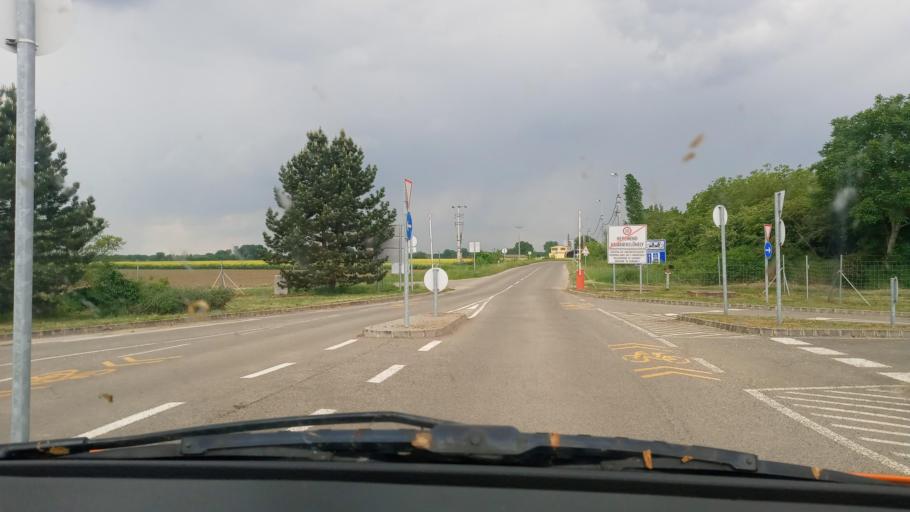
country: HU
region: Baranya
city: Beremend
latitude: 45.7683
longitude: 18.4527
